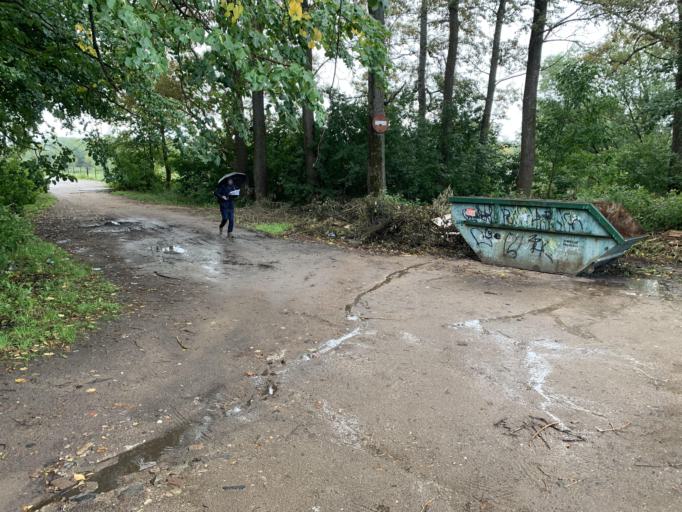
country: RU
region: Tverskaya
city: Vyshniy Volochek
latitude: 57.5819
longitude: 34.5499
